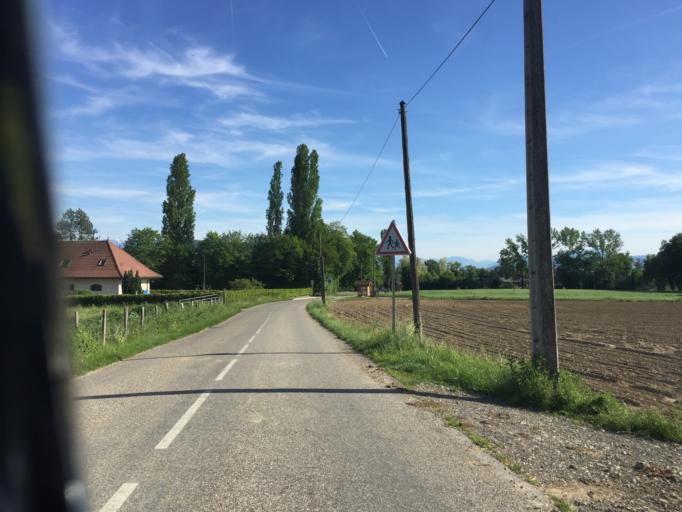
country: FR
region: Rhone-Alpes
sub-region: Departement de la Haute-Savoie
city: Sales
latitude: 45.9105
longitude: 5.9789
